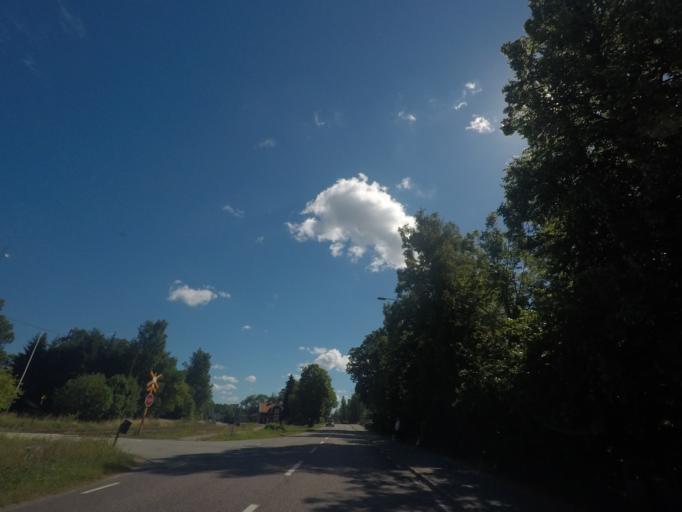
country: SE
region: Stockholm
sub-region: Norrtalje Kommun
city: Nykvarn
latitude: 59.8759
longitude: 18.0418
